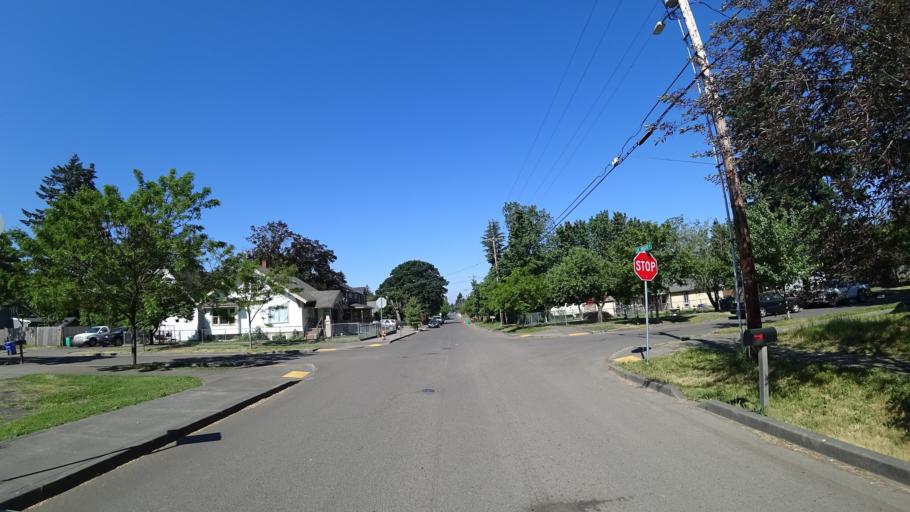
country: US
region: Oregon
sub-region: Multnomah County
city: Lents
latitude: 45.4797
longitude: -122.5556
